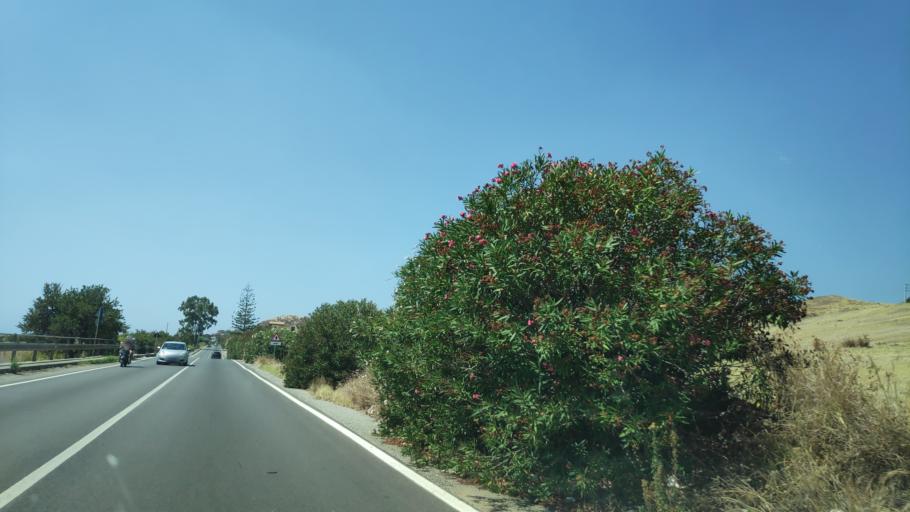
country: IT
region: Calabria
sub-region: Provincia di Reggio Calabria
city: Weather Station
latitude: 37.9564
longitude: 16.0944
